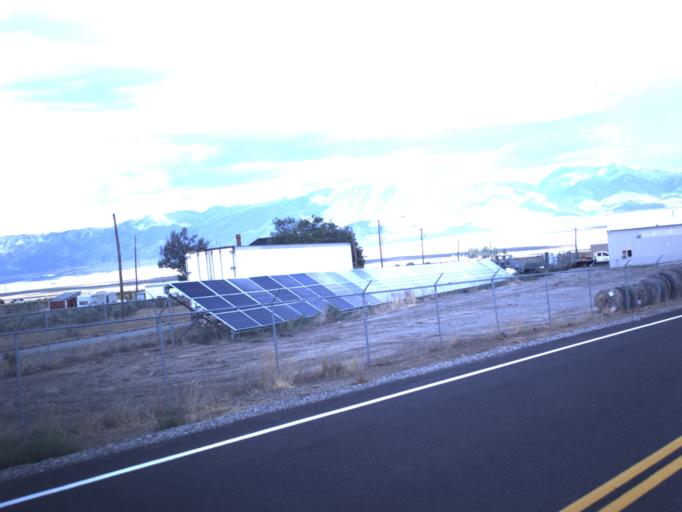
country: US
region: Utah
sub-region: Tooele County
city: Tooele
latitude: 40.3386
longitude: -112.4628
